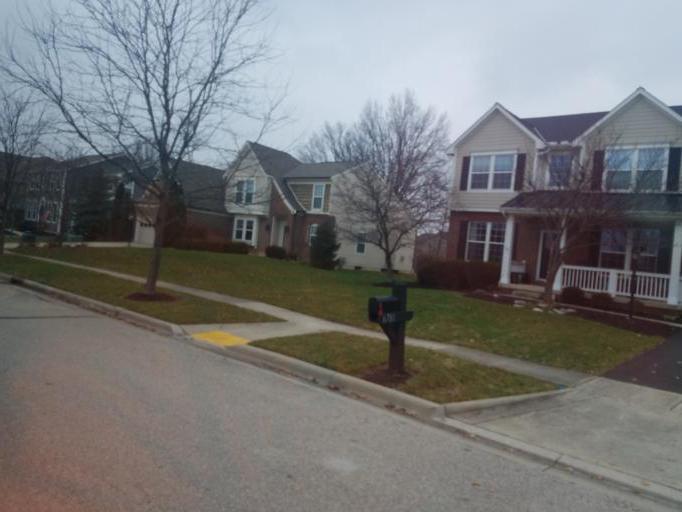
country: US
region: Ohio
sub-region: Franklin County
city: Westerville
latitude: 40.1940
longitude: -82.9203
